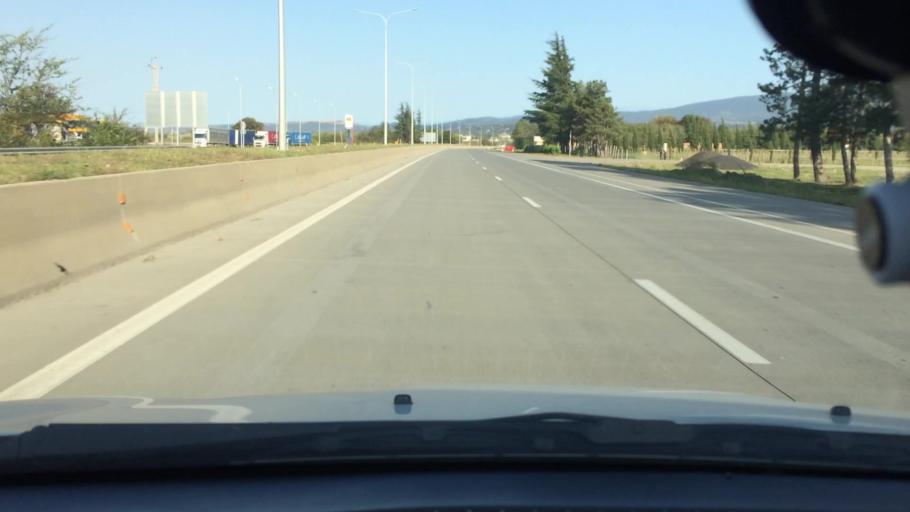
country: GE
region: Imereti
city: Zestap'oni
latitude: 42.1641
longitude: 42.9425
